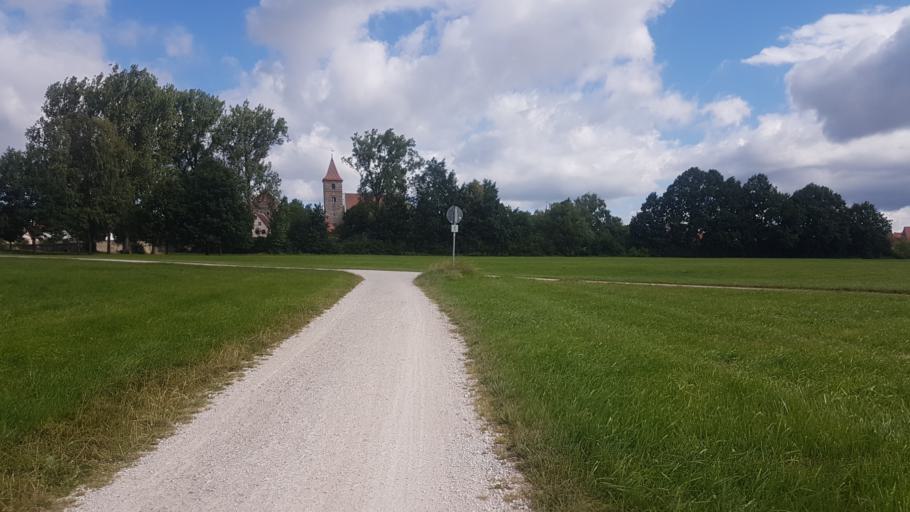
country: DE
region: Bavaria
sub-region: Regierungsbezirk Mittelfranken
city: Ornbau
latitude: 49.1722
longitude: 10.6565
